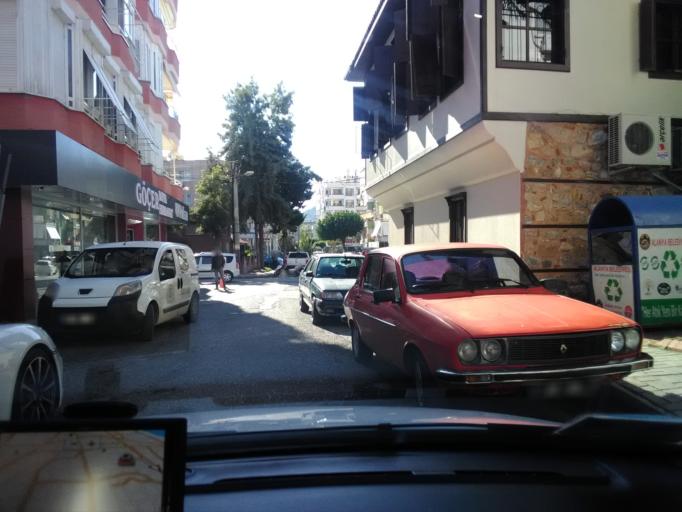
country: TR
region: Antalya
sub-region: Alanya
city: Alanya
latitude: 36.5485
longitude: 32.0003
